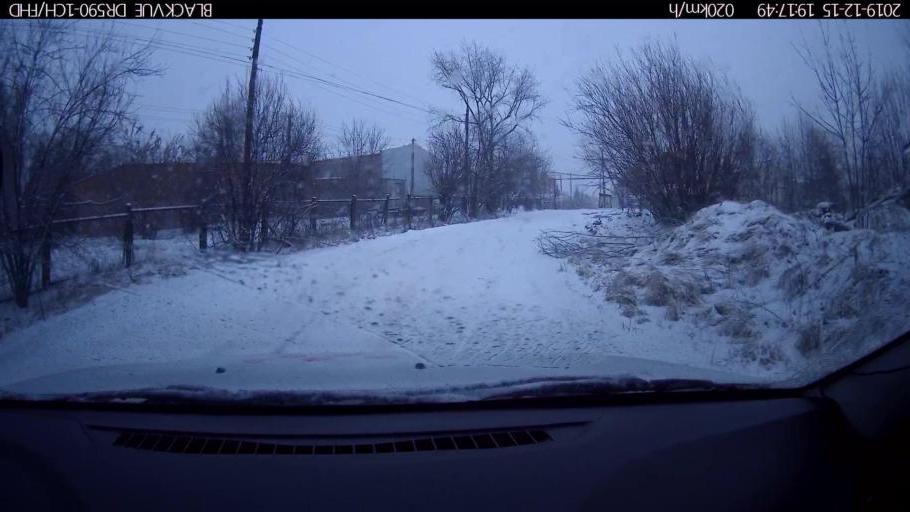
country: RU
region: Nizjnij Novgorod
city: Afonino
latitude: 56.3022
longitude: 44.0864
